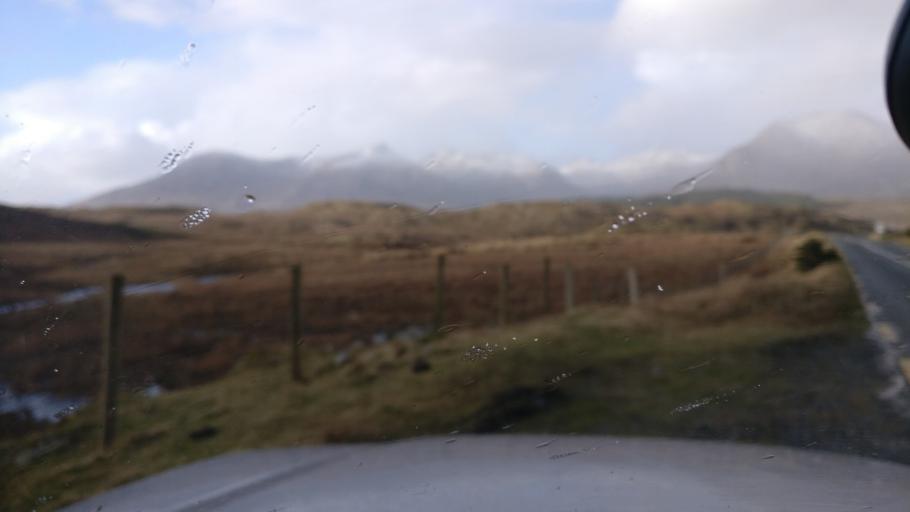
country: IE
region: Connaught
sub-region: County Galway
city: Clifden
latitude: 53.4502
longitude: -9.7723
